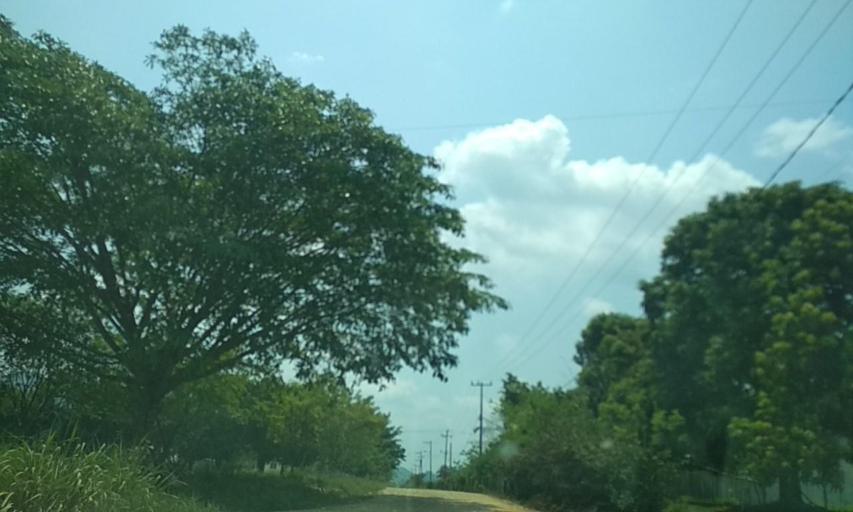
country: MX
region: Chiapas
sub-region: Tecpatan
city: Raudales Malpaso
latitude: 17.3446
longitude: -93.9638
